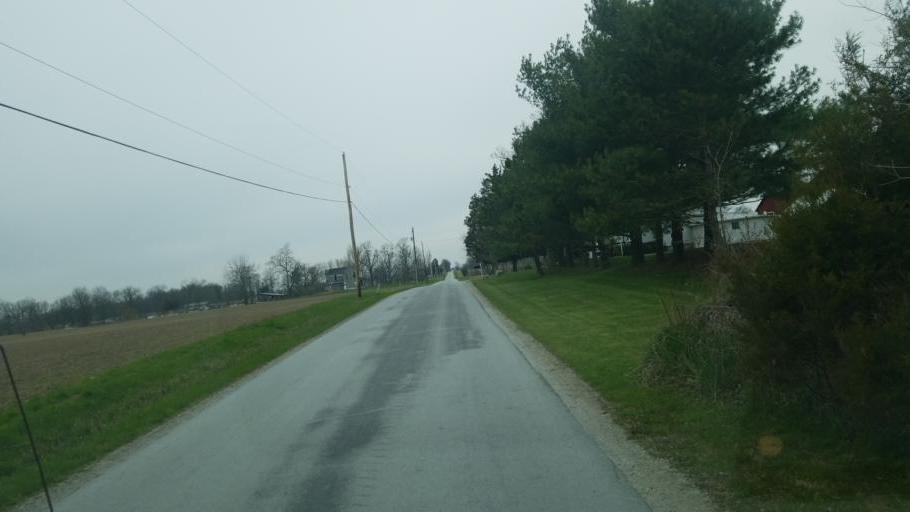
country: US
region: Ohio
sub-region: Hardin County
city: Forest
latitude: 40.8178
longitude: -83.4822
